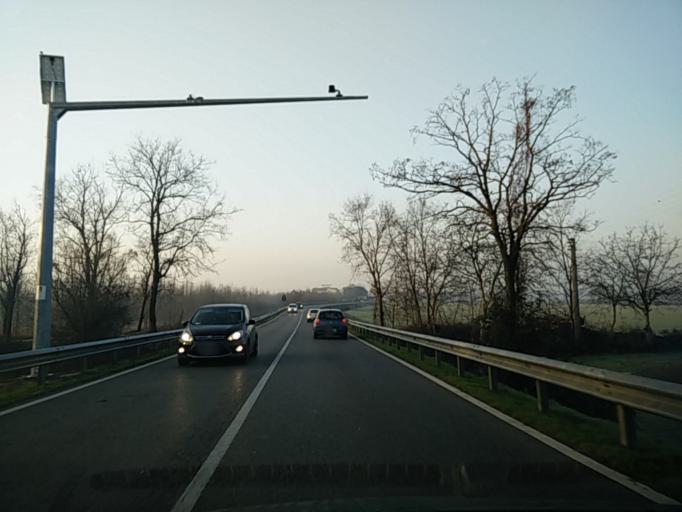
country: IT
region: Veneto
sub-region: Provincia di Venezia
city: Quarto d'Altino
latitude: 45.5372
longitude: 12.3987
